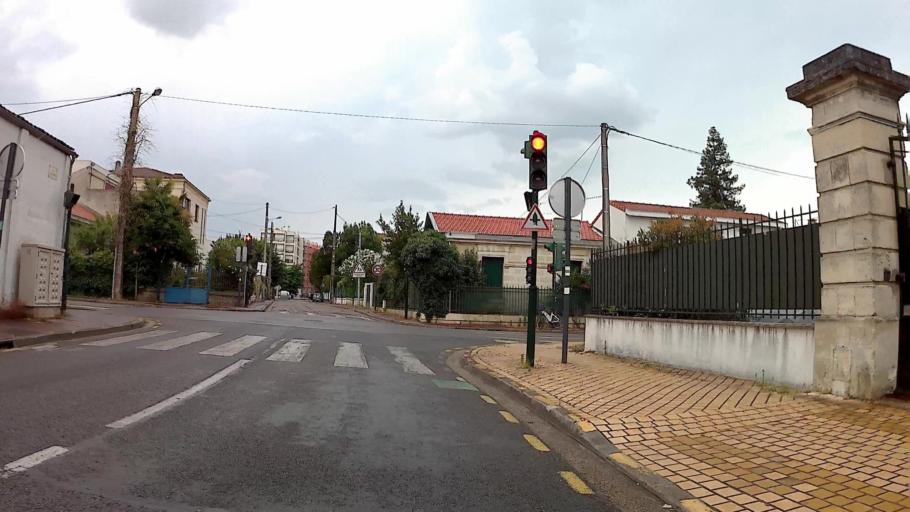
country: FR
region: Aquitaine
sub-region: Departement de la Gironde
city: Le Bouscat
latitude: 44.8587
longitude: -0.6035
